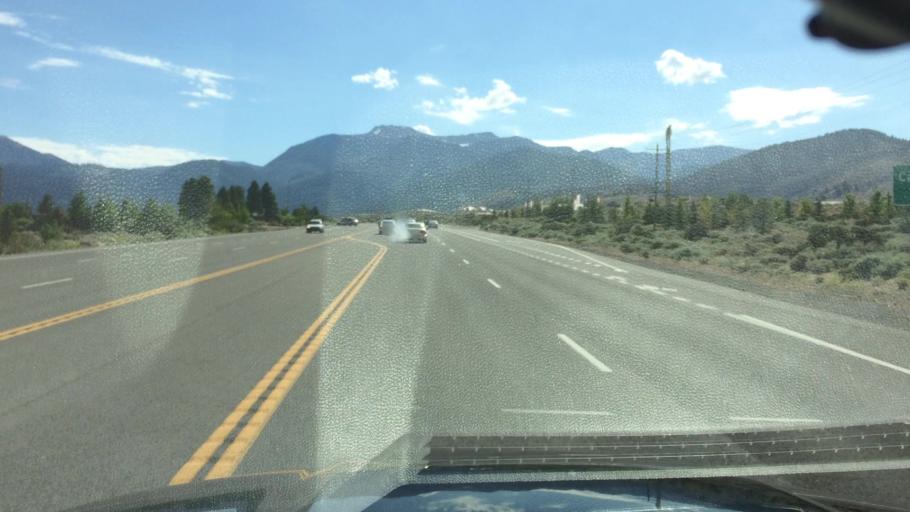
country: US
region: Nevada
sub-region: Washoe County
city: Reno
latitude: 39.3861
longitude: -119.8131
